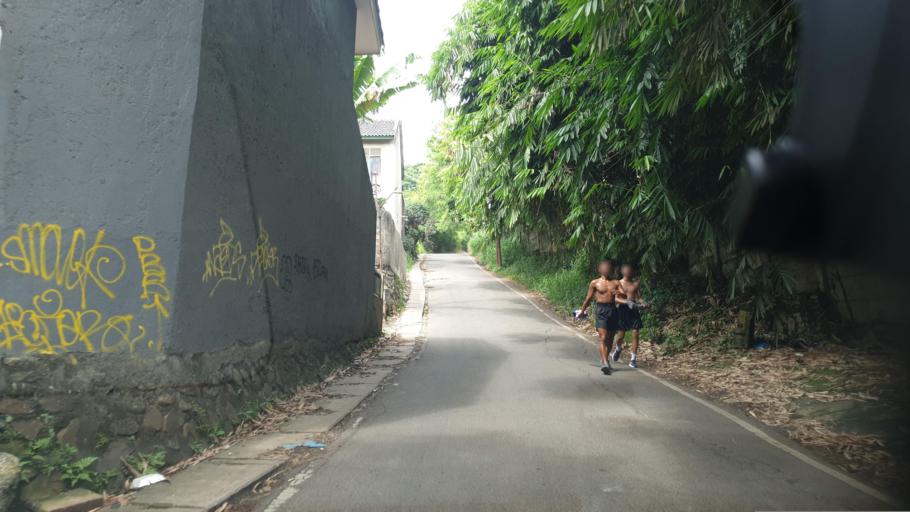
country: ID
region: West Java
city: Pamulang
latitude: -6.3482
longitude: 106.7734
